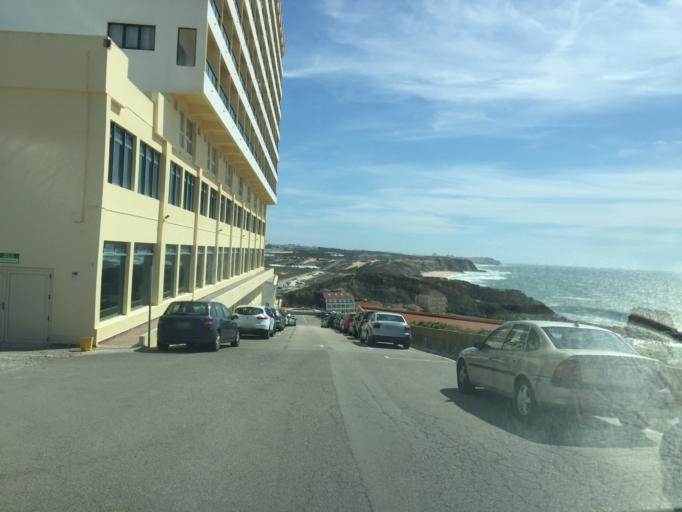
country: PT
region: Lisbon
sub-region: Torres Vedras
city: A dos Cunhados
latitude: 39.1803
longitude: -9.3550
